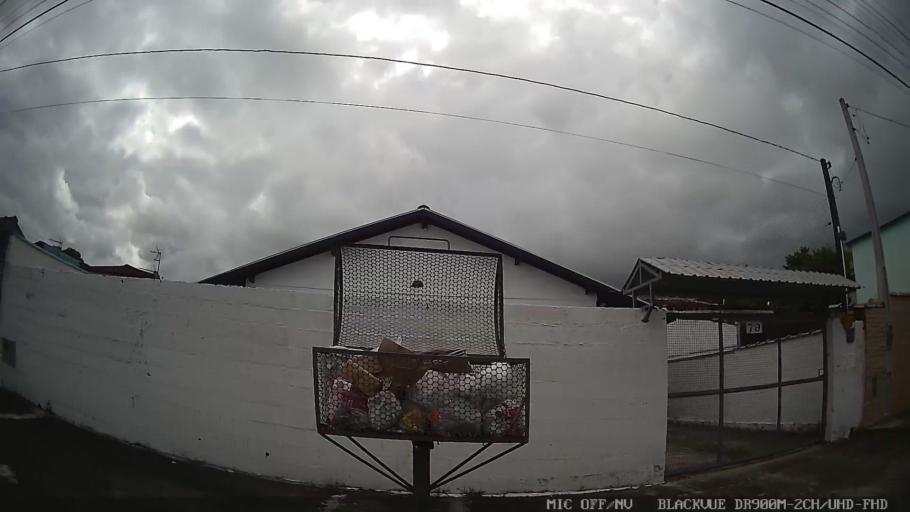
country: BR
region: Sao Paulo
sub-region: Caraguatatuba
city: Caraguatatuba
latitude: -23.6412
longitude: -45.4396
